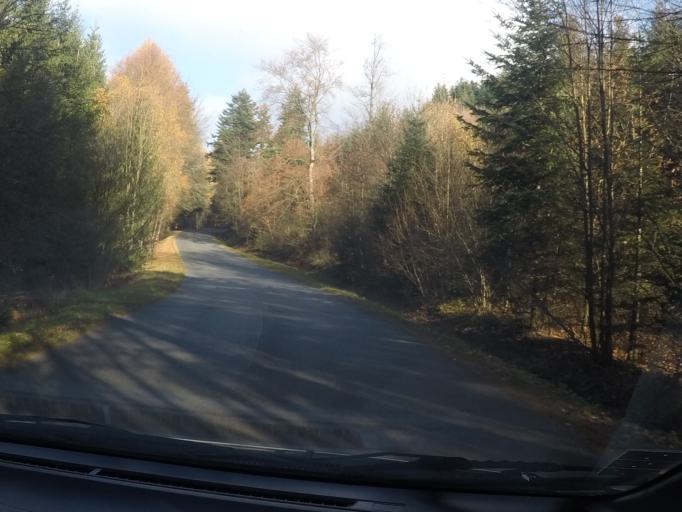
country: SK
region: Banskobystricky
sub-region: Okres Banska Bystrica
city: Banska Stiavnica
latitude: 48.4695
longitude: 18.8727
